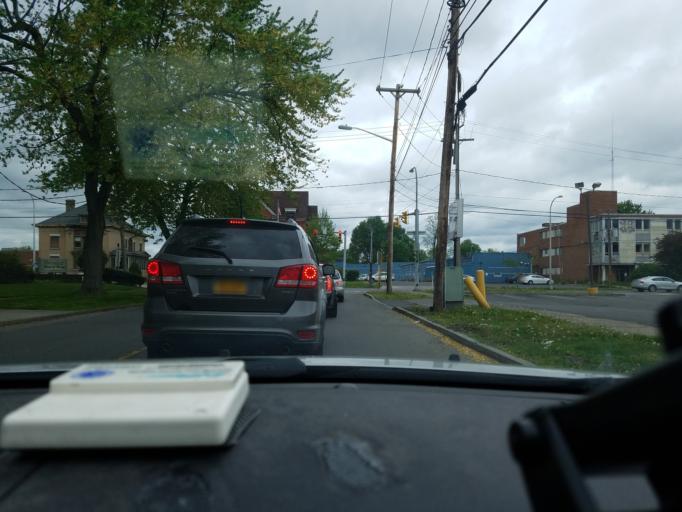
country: US
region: New York
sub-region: Onondaga County
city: Syracuse
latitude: 43.0398
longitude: -76.1578
